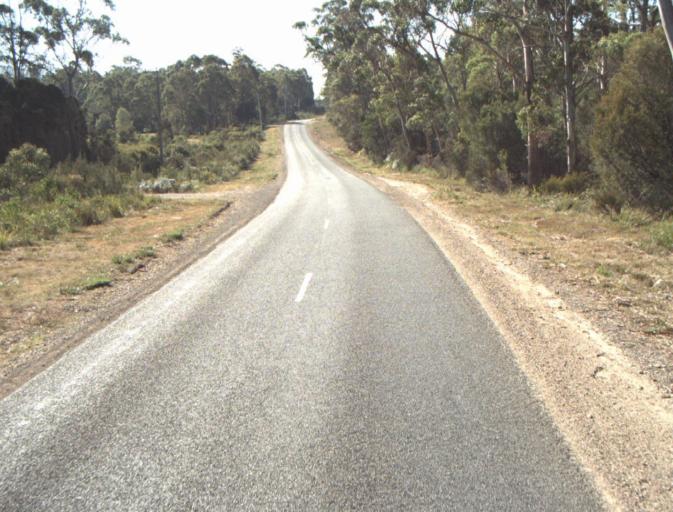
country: AU
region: Tasmania
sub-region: Launceston
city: Mayfield
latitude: -41.3056
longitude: 147.1337
